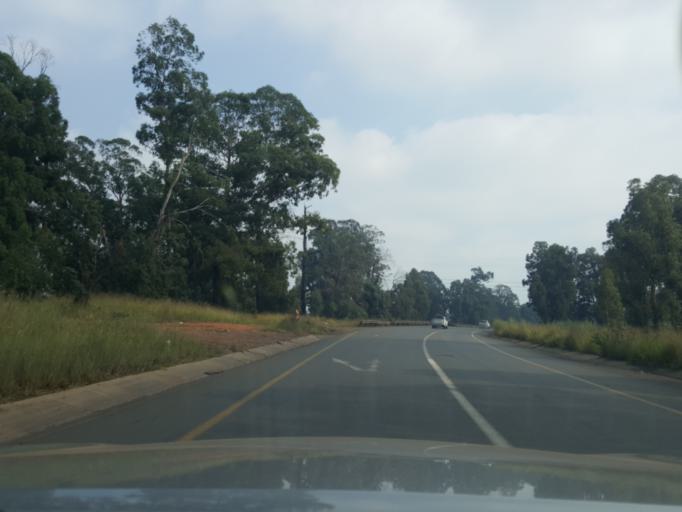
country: ZA
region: Mpumalanga
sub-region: Nkangala District Municipality
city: Witbank
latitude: -25.9993
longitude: 29.2913
